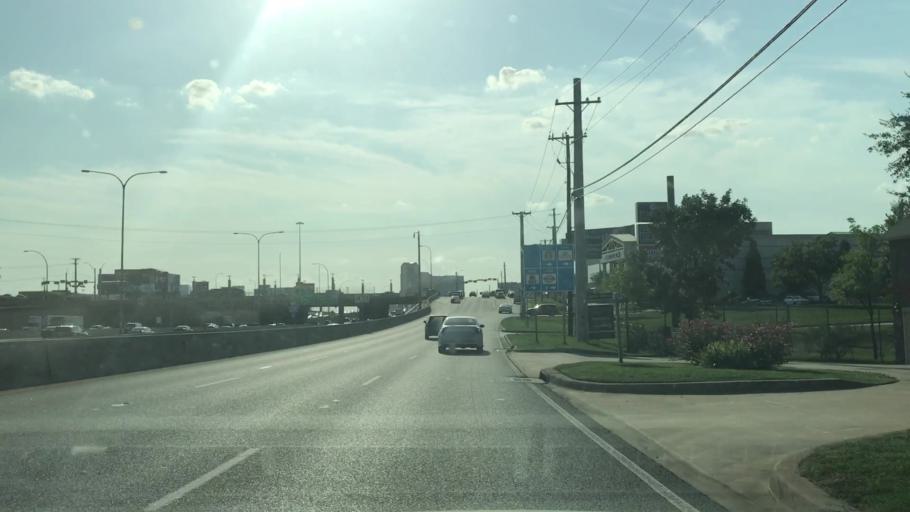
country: US
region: Texas
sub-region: Dallas County
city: Addison
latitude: 32.9256
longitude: -96.8007
